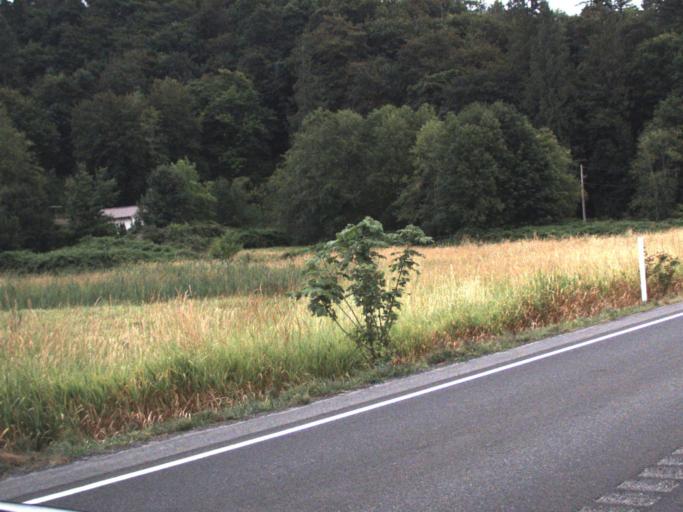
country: US
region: Washington
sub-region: King County
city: Fall City
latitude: 47.5893
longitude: -121.9043
